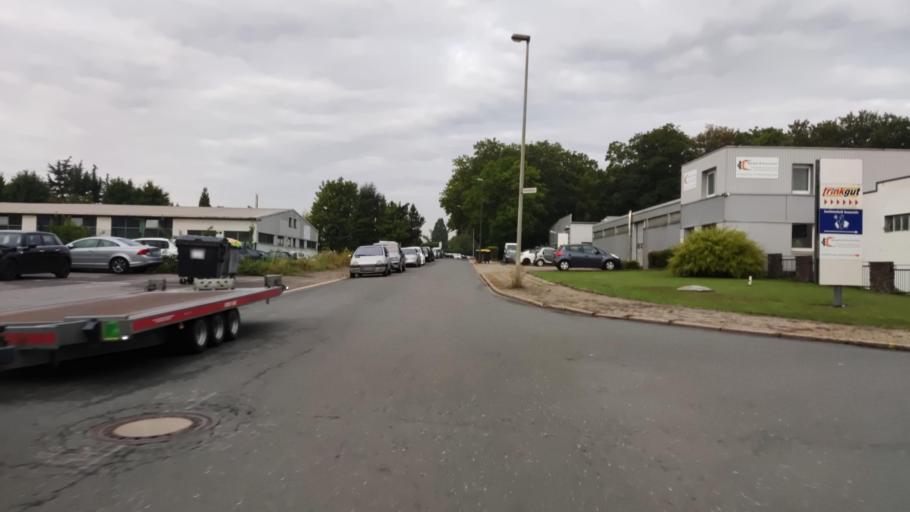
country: DE
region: North Rhine-Westphalia
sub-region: Regierungsbezirk Arnsberg
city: Herne
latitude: 51.5473
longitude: 7.2399
